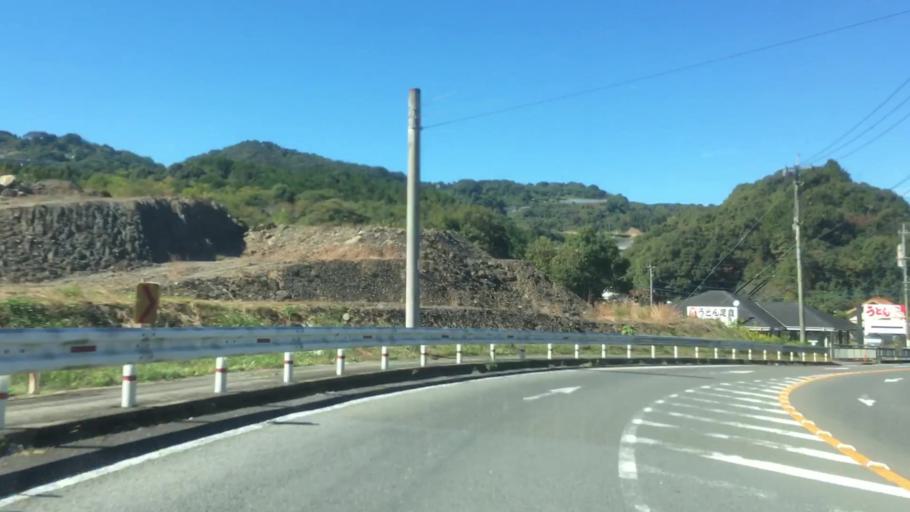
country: JP
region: Nagasaki
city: Sasebo
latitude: 32.9938
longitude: 129.7337
